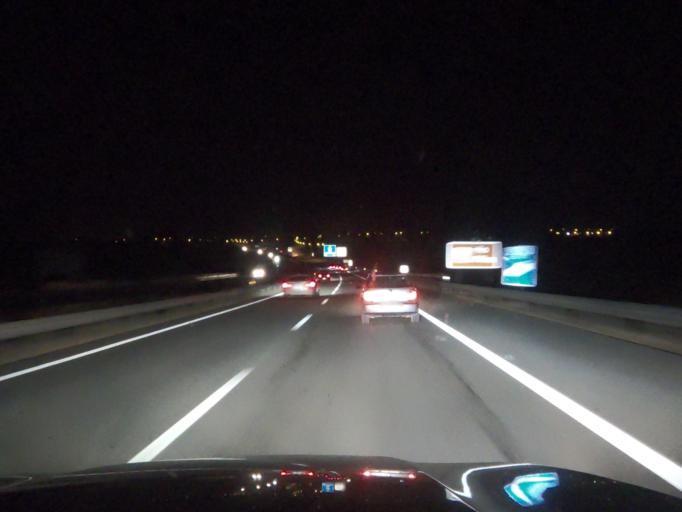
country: PT
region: Beja
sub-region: Almodovar
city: Almodovar
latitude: 37.5122
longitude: -8.1847
